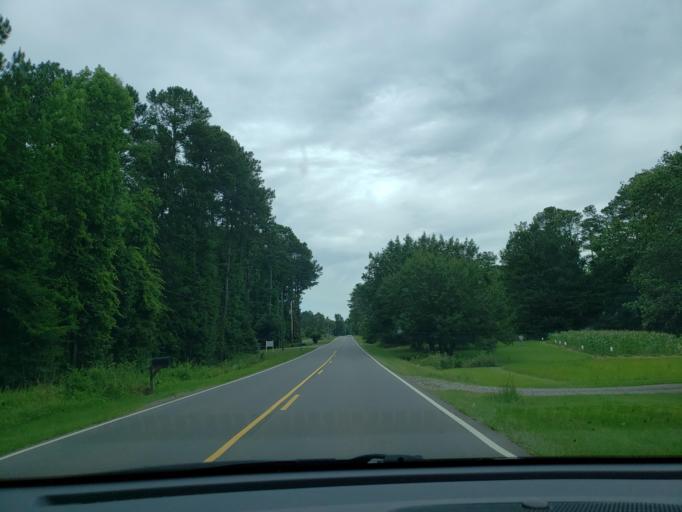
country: US
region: North Carolina
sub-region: Wake County
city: Green Level
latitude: 35.7316
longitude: -79.0024
